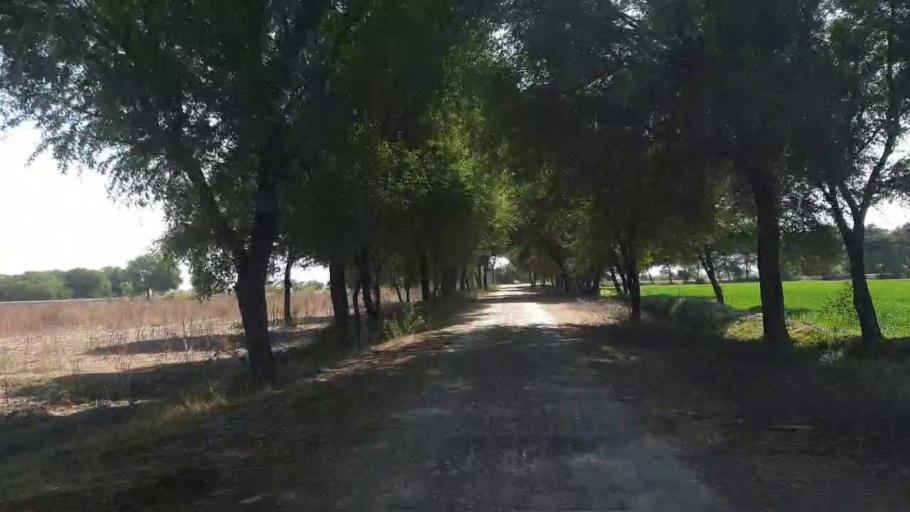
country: PK
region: Sindh
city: Chambar
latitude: 25.2900
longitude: 68.6859
